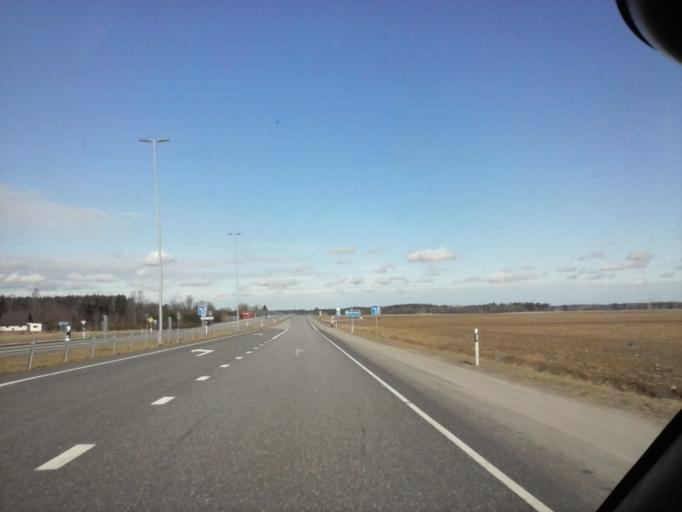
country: EE
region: Harju
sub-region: Raasiku vald
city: Raasiku
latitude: 59.1716
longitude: 25.1556
